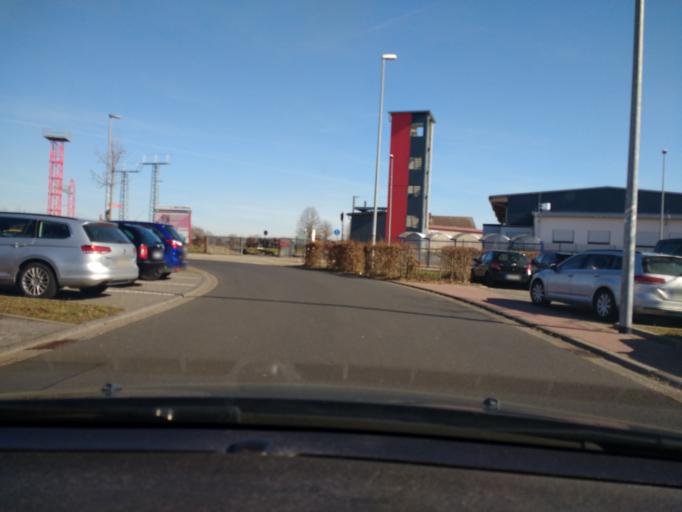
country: DE
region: Bavaria
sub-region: Regierungsbezirk Unterfranken
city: Geiselbach
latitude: 50.1403
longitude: 9.1265
